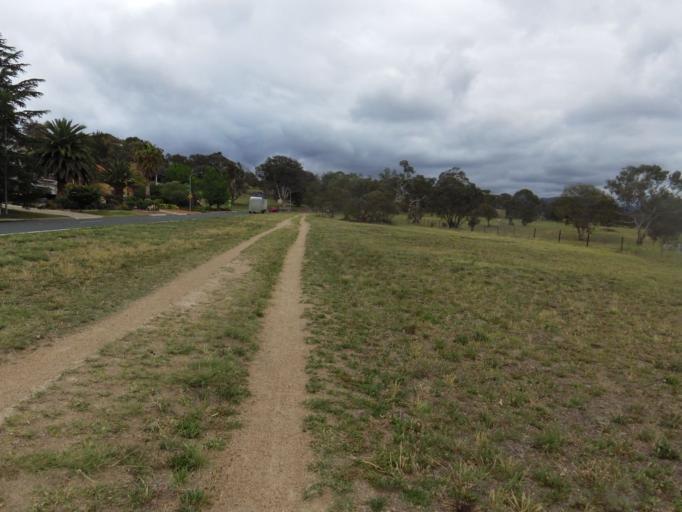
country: AU
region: Australian Capital Territory
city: Macquarie
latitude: -35.3491
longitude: 149.0251
